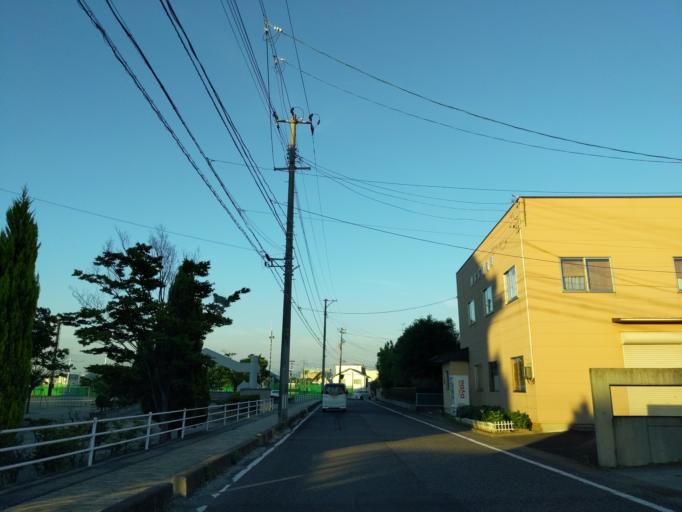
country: JP
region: Fukushima
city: Koriyama
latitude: 37.4164
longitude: 140.3359
